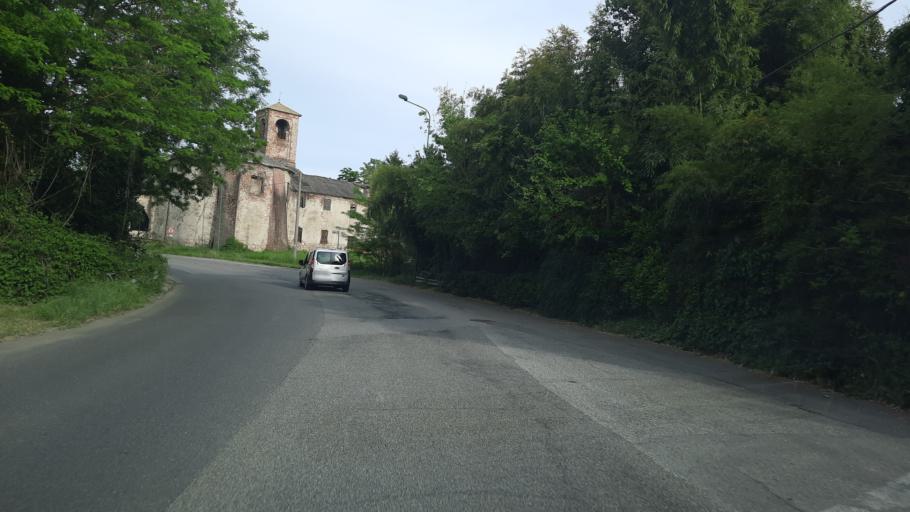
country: IT
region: Piedmont
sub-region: Provincia di Alessandria
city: Casale Monferrato
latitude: 45.1337
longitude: 8.4284
